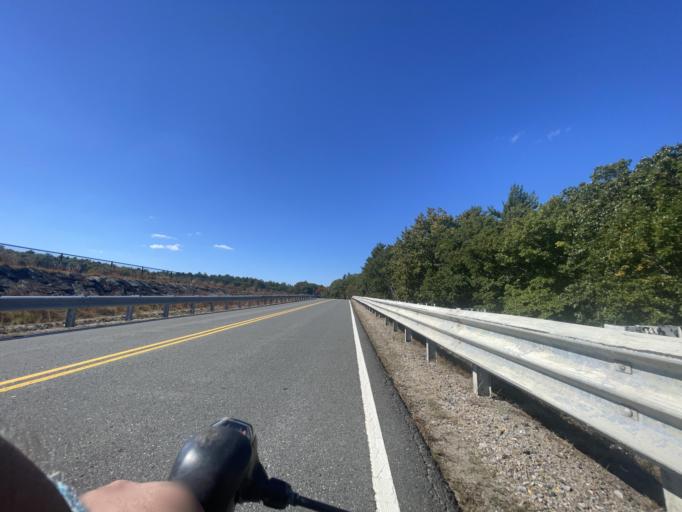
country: US
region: Massachusetts
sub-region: Norfolk County
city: Milton
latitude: 42.2289
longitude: -71.0492
